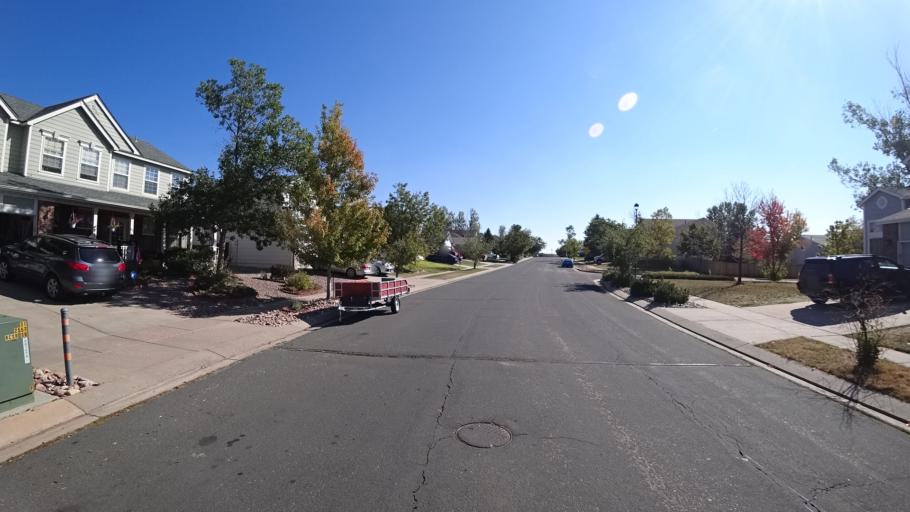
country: US
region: Colorado
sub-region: El Paso County
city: Cimarron Hills
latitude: 38.8851
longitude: -104.7081
